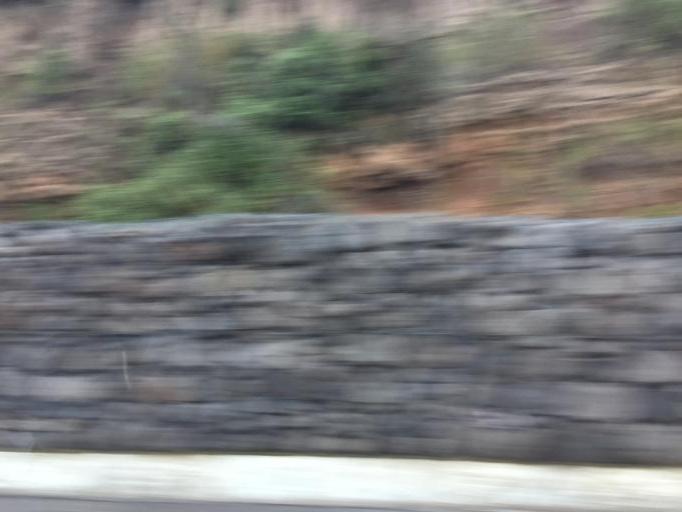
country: MX
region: Michoacan
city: Panindicuaro de la Reforma
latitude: 19.9675
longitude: -101.7082
